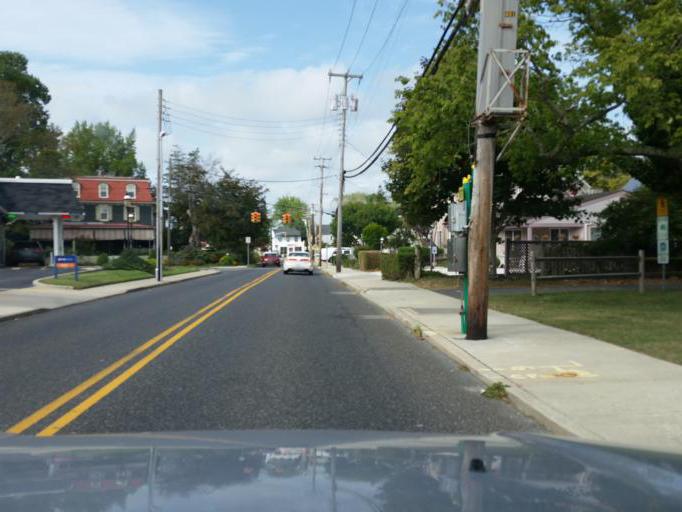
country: US
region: New Jersey
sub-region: Cape May County
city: Cape May
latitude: 38.9384
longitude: -74.9160
